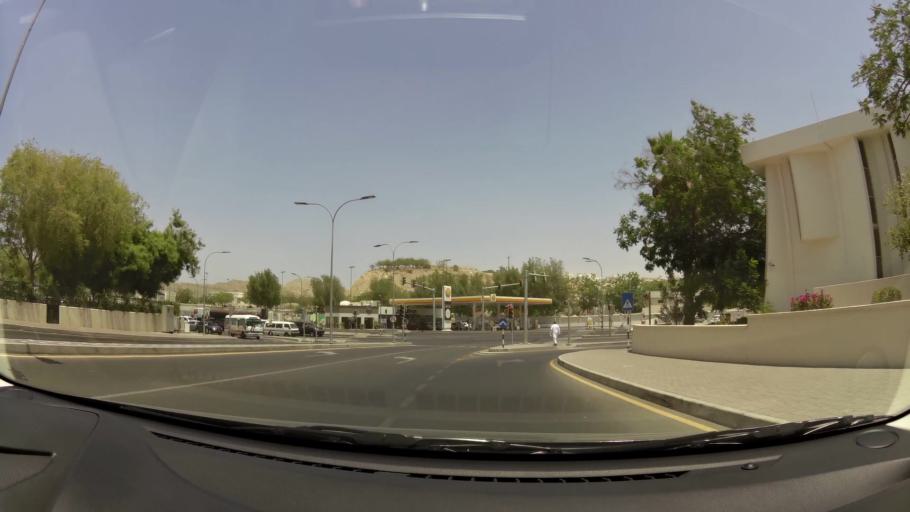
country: OM
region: Muhafazat Masqat
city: Muscat
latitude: 23.6232
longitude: 58.5063
